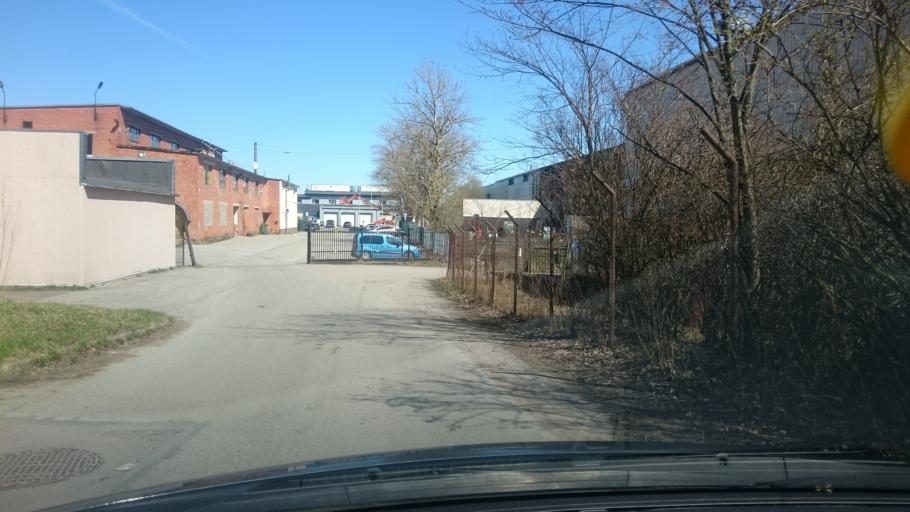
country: EE
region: Harju
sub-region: Tallinna linn
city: Tallinn
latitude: 59.4575
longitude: 24.6890
